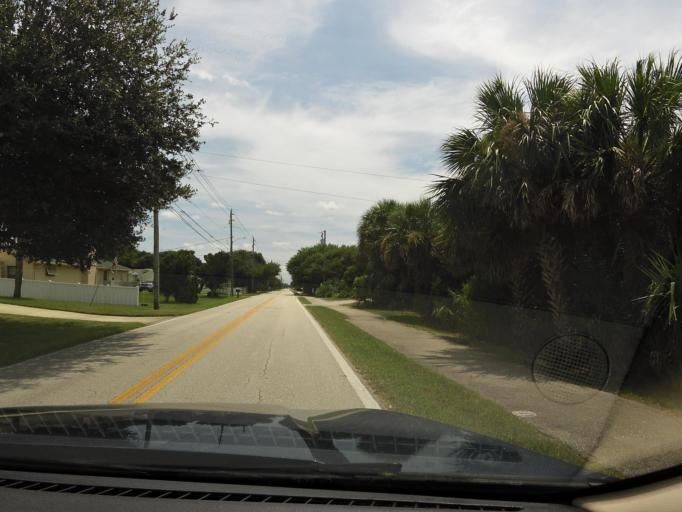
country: US
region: Florida
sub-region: Volusia County
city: Ponce Inlet
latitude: 29.1084
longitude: -80.9463
